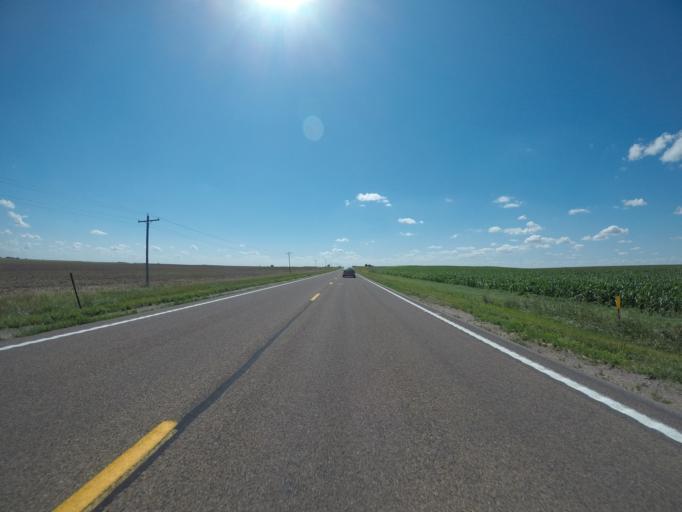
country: US
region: Nebraska
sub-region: Chase County
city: Imperial
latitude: 40.5375
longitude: -101.8218
